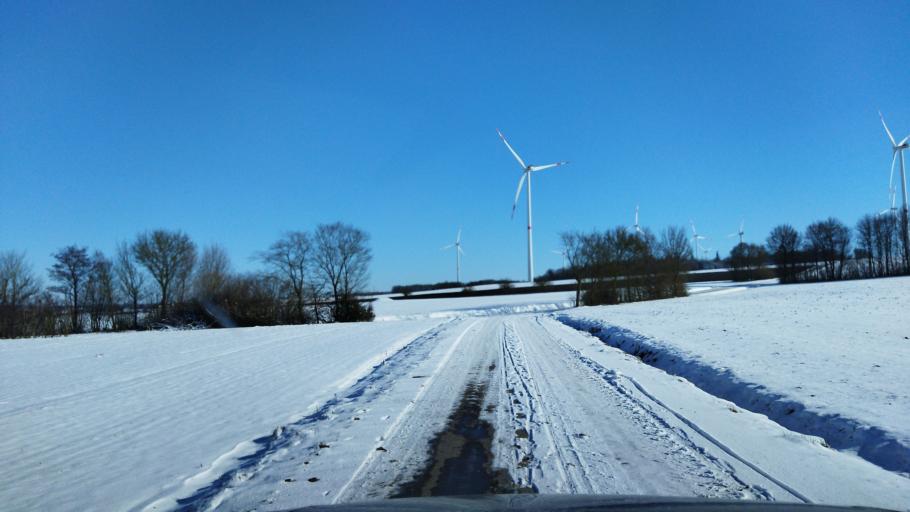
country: DE
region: Baden-Wuerttemberg
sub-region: Regierungsbezirk Stuttgart
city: Ilshofen
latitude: 49.1932
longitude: 9.9388
